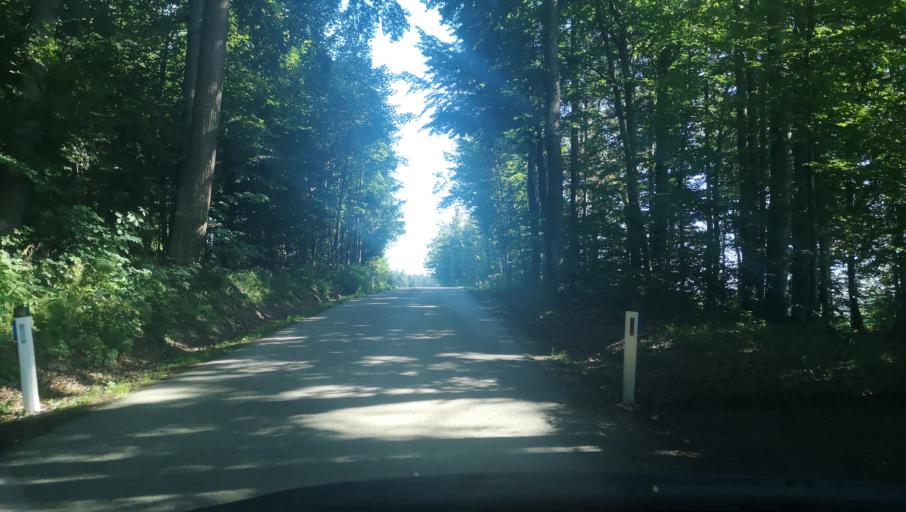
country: AT
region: Lower Austria
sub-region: Politischer Bezirk Melk
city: Blindenmarkt
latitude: 48.1425
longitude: 15.0003
